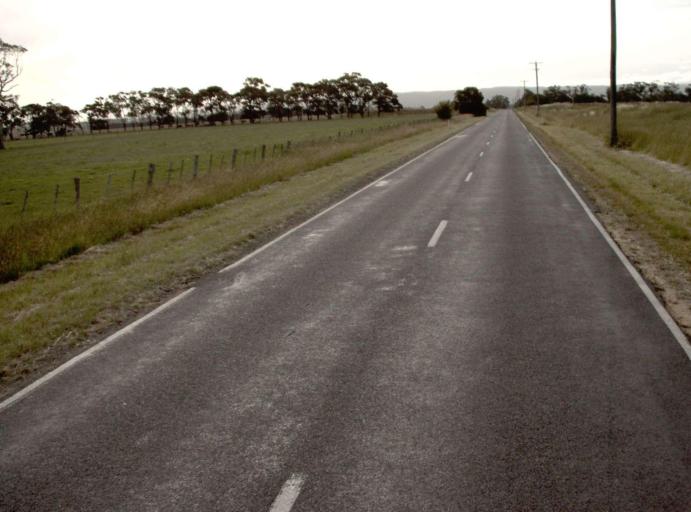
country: AU
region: Victoria
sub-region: Wellington
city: Heyfield
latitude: -38.0198
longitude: 146.7487
